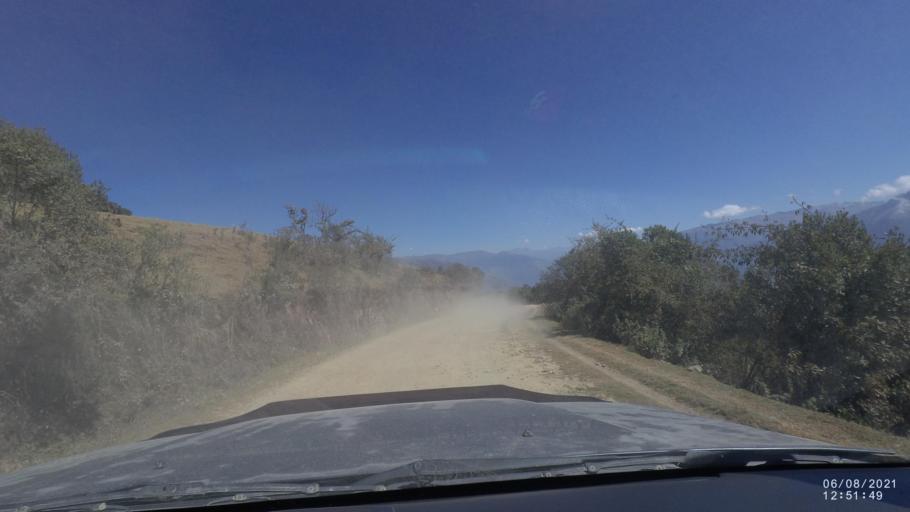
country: BO
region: Cochabamba
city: Colchani
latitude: -16.7614
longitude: -66.6809
